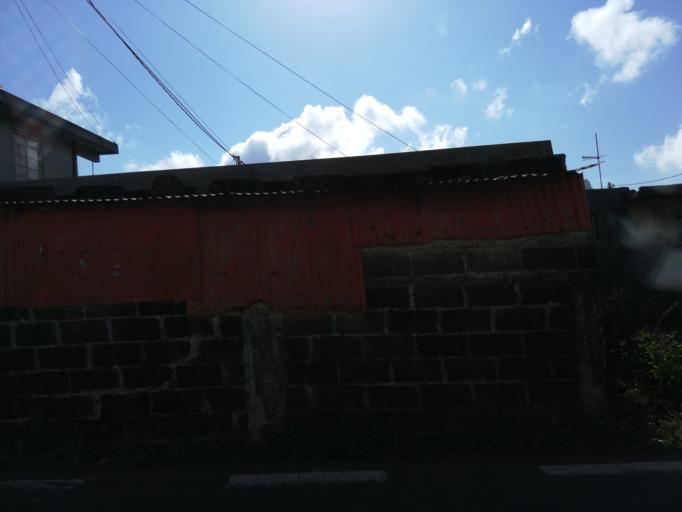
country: MU
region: Pamplemousses
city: Creve Coeur
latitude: -20.2072
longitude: 57.5670
